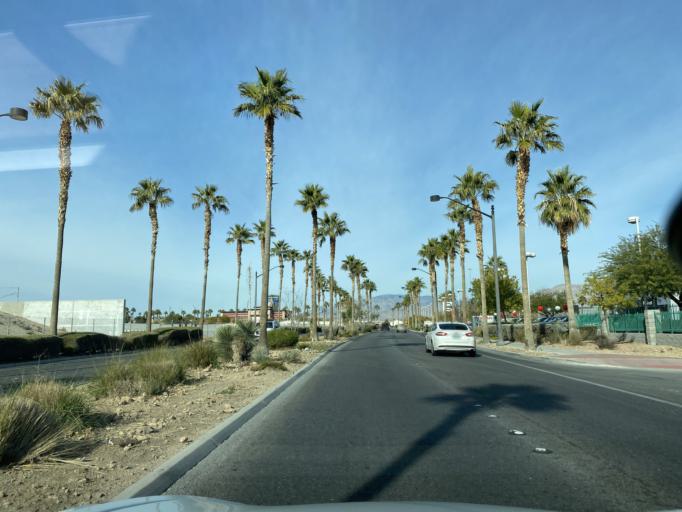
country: US
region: Nevada
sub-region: Clark County
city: Las Vegas
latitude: 36.2671
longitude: -115.2607
